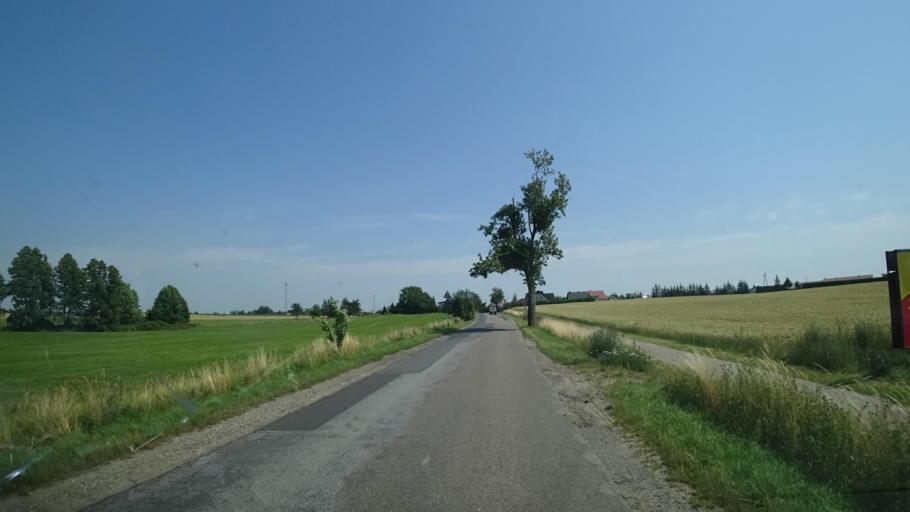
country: PL
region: Pomeranian Voivodeship
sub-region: Powiat chojnicki
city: Brusy
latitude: 53.8829
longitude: 17.7012
